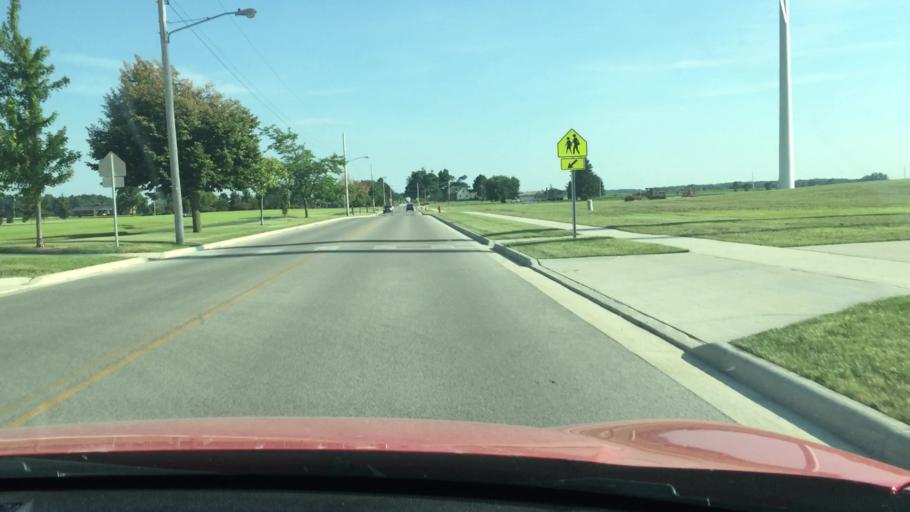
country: US
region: Ohio
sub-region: Hardin County
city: Ada
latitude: 40.7653
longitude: -83.8424
